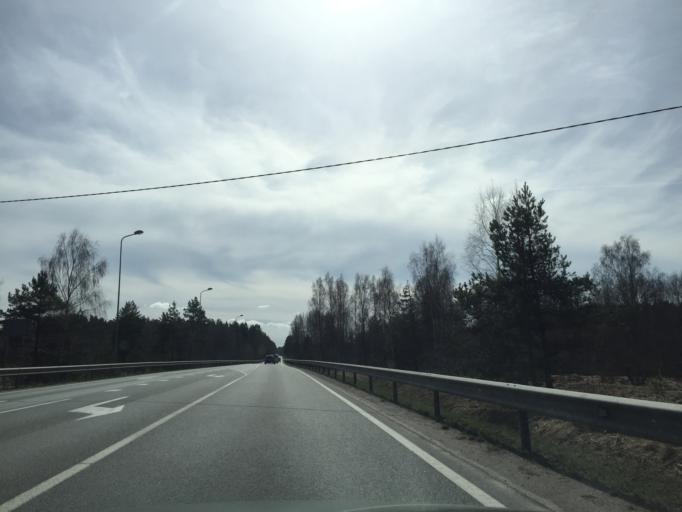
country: LV
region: Salaspils
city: Salaspils
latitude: 56.9421
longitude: 24.3827
